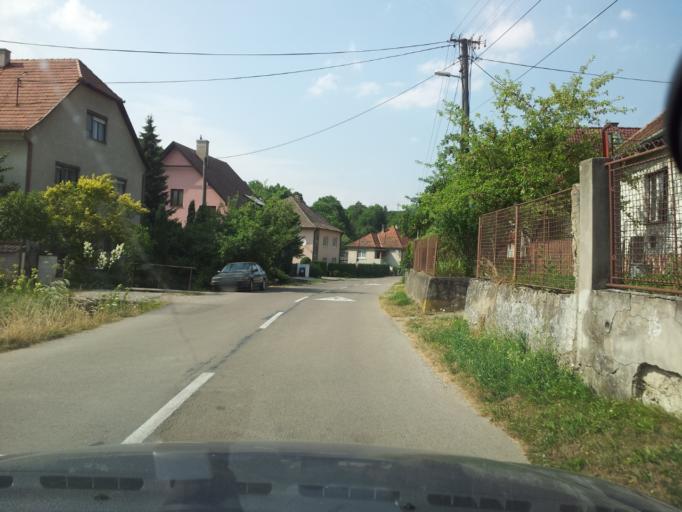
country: SK
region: Trenciansky
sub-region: Okres Trencin
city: Trencin
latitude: 48.8766
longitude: 18.1007
